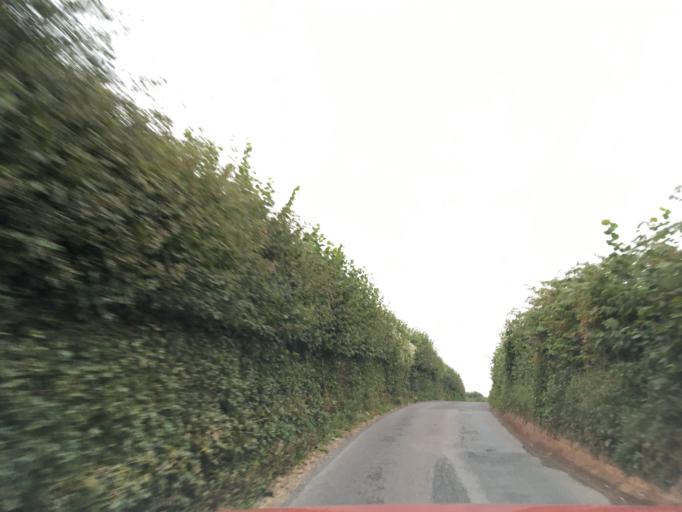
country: GB
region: Wales
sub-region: Newport
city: Langstone
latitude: 51.6175
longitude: -2.9075
